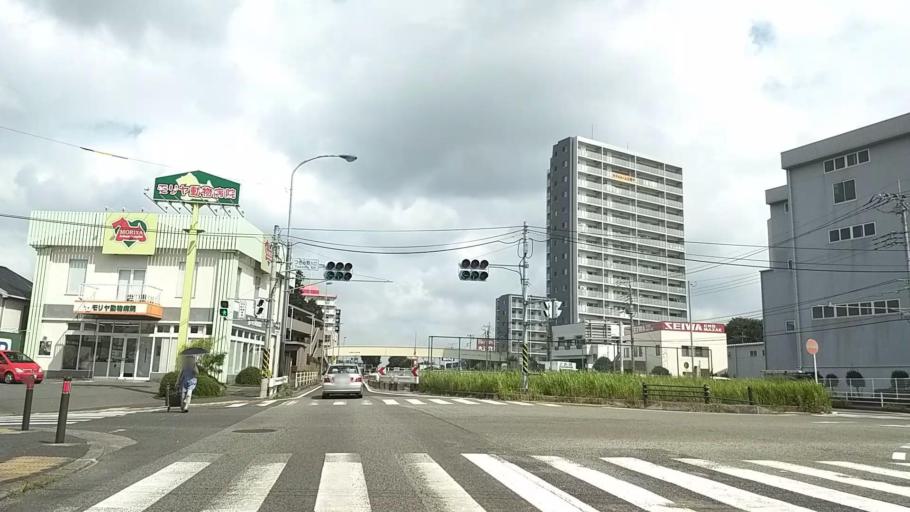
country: JP
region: Tokyo
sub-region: Machida-shi
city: Machida
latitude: 35.5162
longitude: 139.4556
